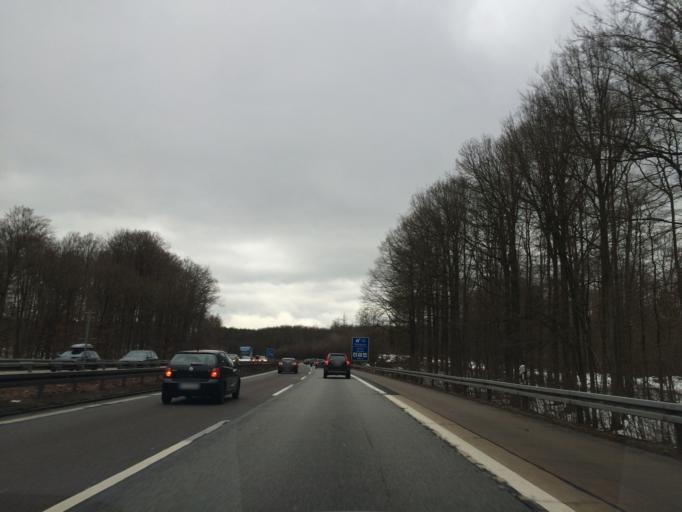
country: DE
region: Bavaria
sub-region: Regierungsbezirk Unterfranken
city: Weibersbrunn
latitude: 49.9062
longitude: 9.3734
